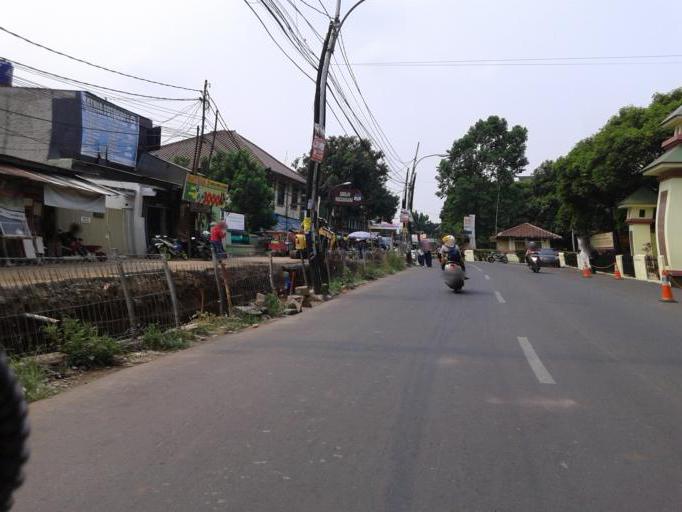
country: ID
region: West Java
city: Pamulang
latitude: -6.3111
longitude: 106.7589
